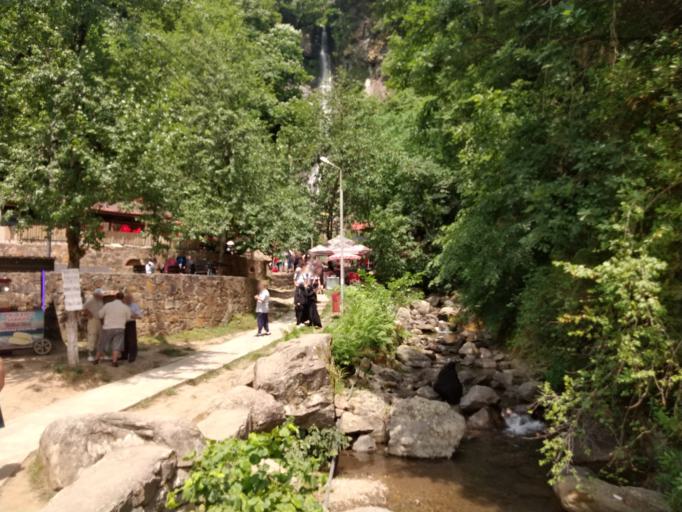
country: GE
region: Ajaria
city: Keda
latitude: 41.5741
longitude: 41.8590
